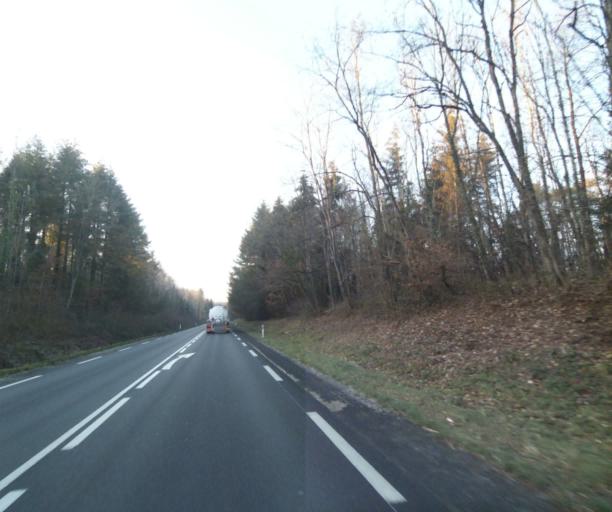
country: FR
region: Champagne-Ardenne
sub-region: Departement de la Haute-Marne
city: Bienville
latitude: 48.5630
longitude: 5.0406
